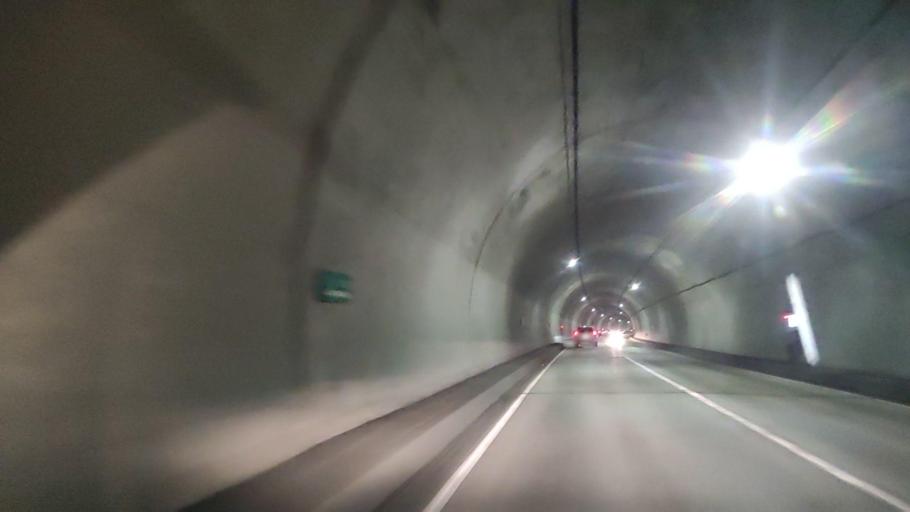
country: JP
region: Hokkaido
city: Ishikari
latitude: 43.5220
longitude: 141.3927
